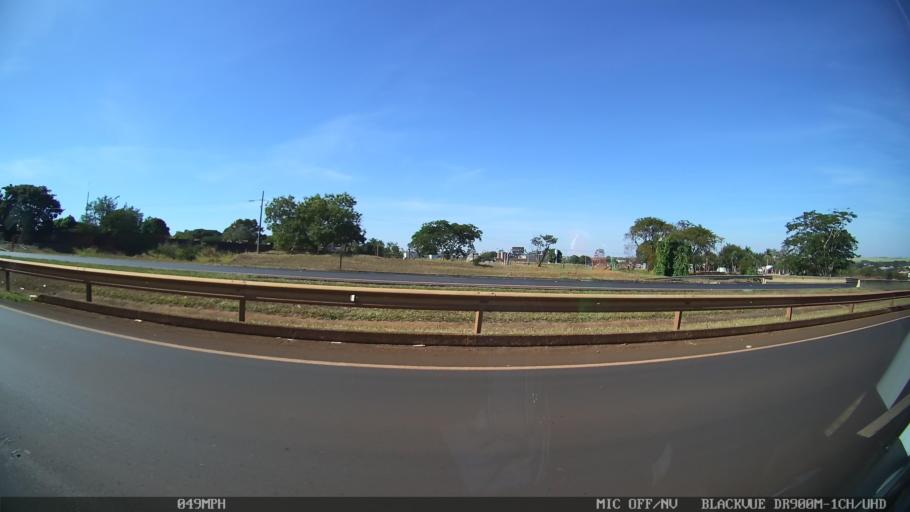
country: BR
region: Sao Paulo
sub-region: Barretos
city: Barretos
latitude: -20.5820
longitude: -48.5807
